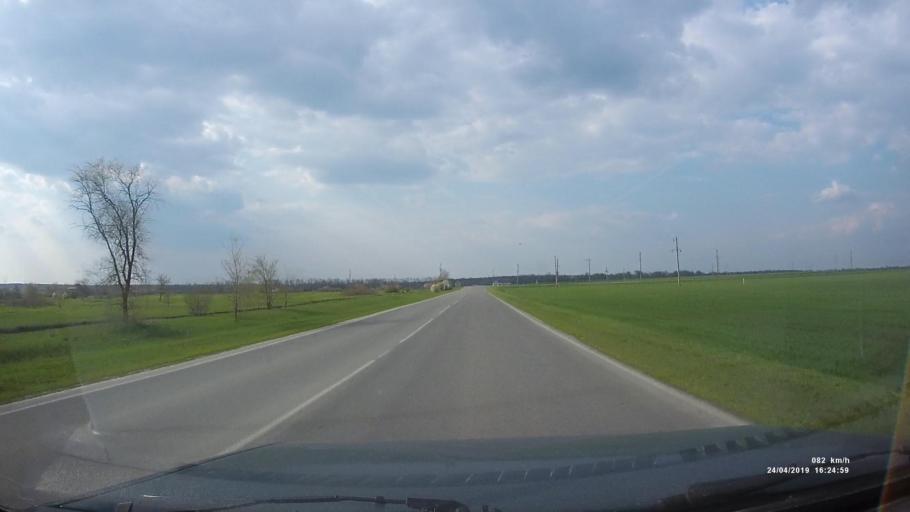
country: RU
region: Rostov
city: Orlovskiy
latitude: 46.8475
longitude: 42.0444
